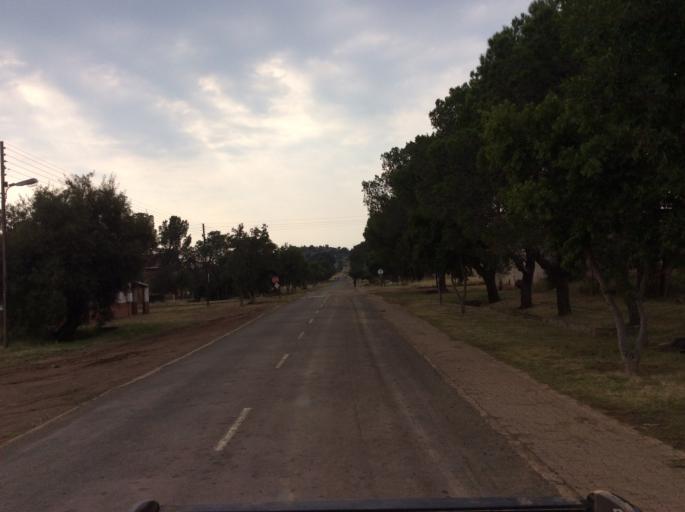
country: LS
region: Mafeteng
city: Mafeteng
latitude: -29.9874
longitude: 27.0151
